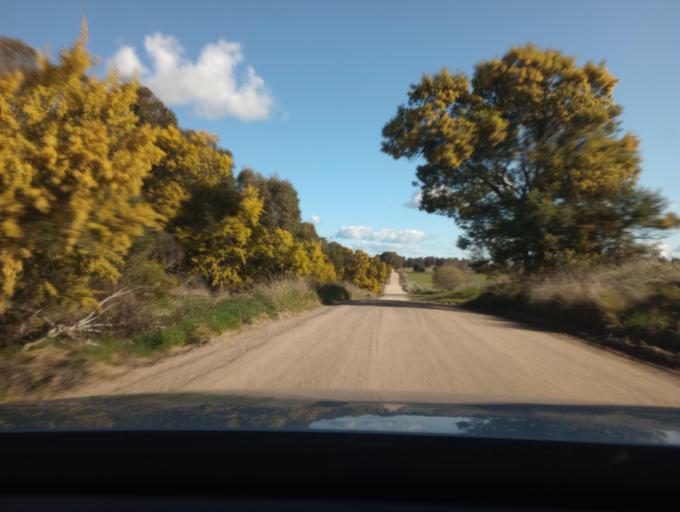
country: AU
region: New South Wales
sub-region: Blayney
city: Millthorpe
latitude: -33.4038
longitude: 149.3078
